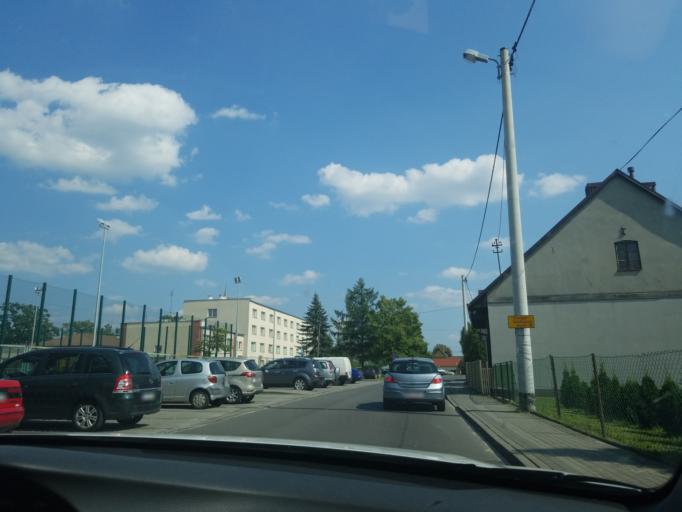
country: PL
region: Subcarpathian Voivodeship
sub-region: Powiat nizanski
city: Nisko
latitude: 50.5183
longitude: 22.1384
